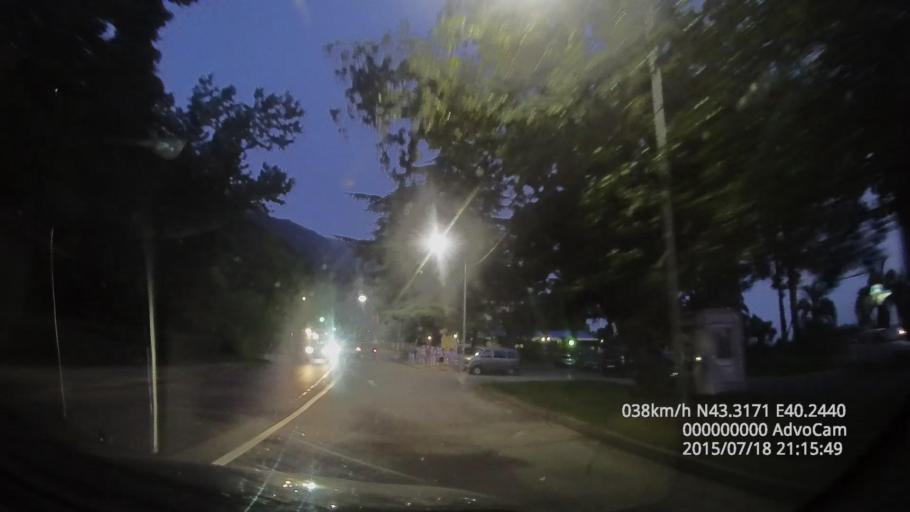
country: GE
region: Abkhazia
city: Gagra
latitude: 43.3170
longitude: 40.2442
